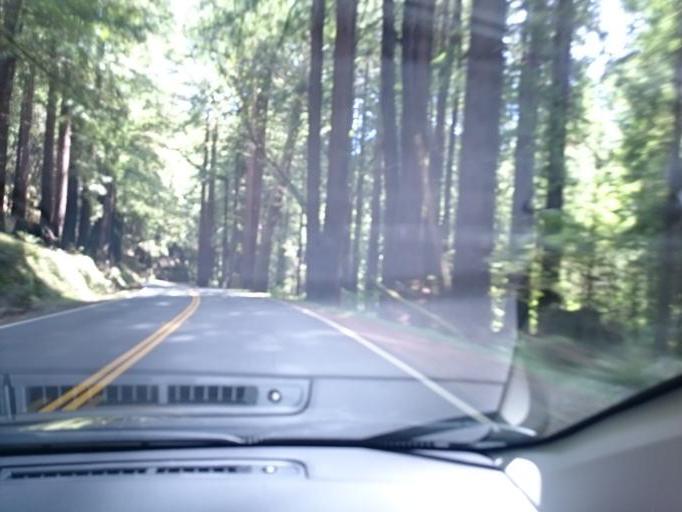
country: US
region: California
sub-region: Mendocino County
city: Fort Bragg
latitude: 39.1792
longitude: -123.7084
